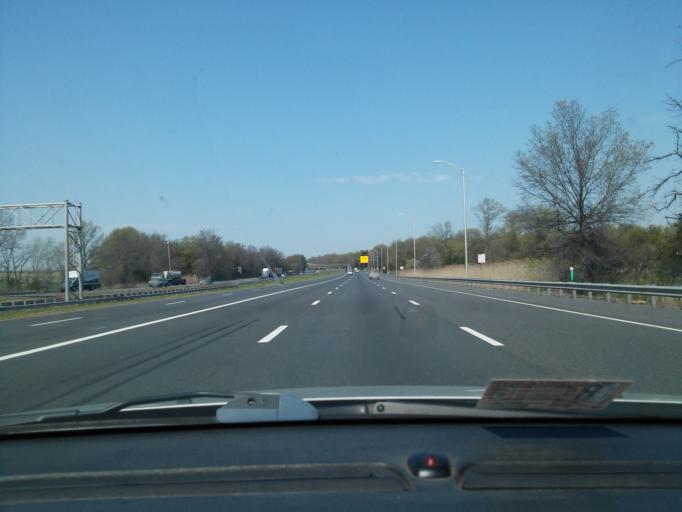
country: US
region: New Jersey
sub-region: Somerset County
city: Bedminster
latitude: 40.6440
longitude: -74.6591
